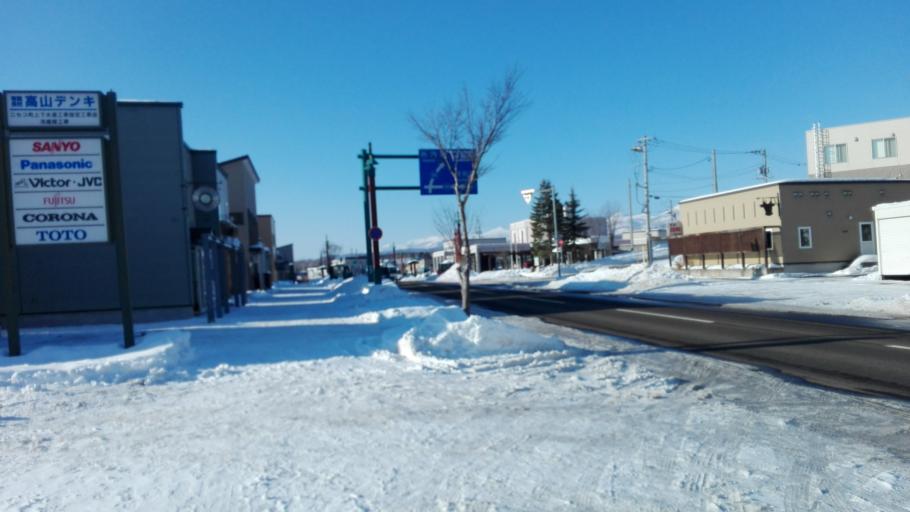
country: JP
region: Hokkaido
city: Niseko Town
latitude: 42.8034
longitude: 140.6875
